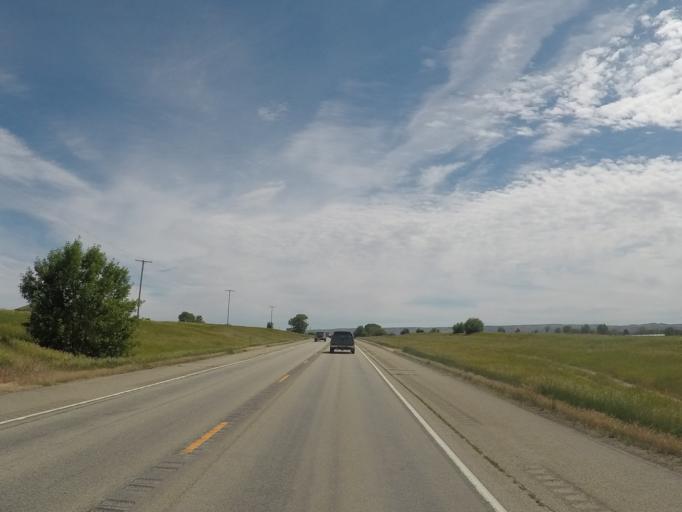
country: US
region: Montana
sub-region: Yellowstone County
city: Laurel
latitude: 45.4968
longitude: -108.9420
